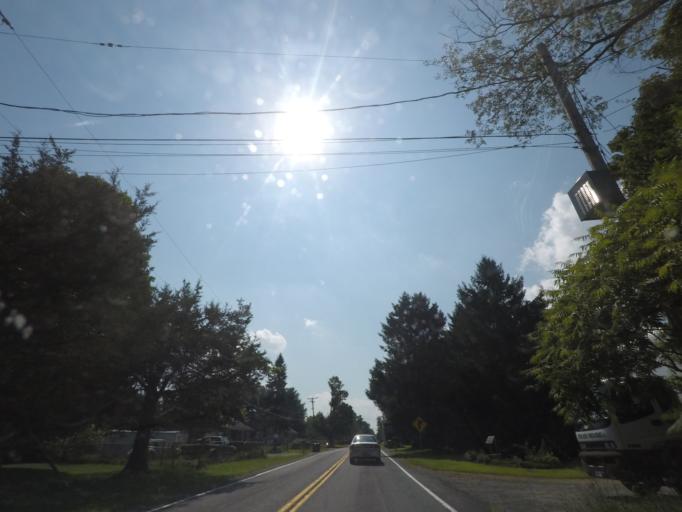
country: US
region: New York
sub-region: Rensselaer County
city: Poestenkill
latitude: 42.8135
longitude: -73.5059
